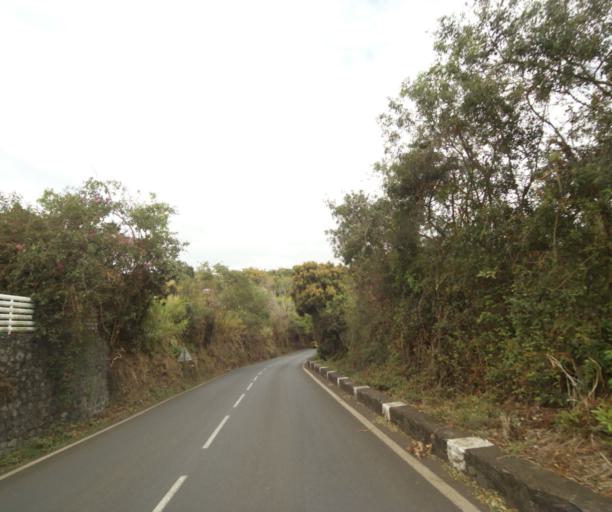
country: RE
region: Reunion
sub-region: Reunion
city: Saint-Paul
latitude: -21.0554
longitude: 55.2833
